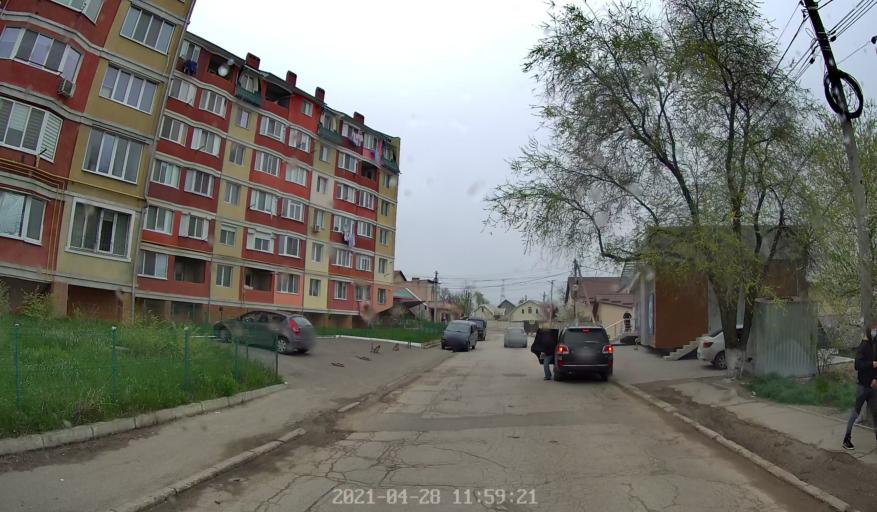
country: MD
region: Chisinau
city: Singera
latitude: 46.9829
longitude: 28.9333
